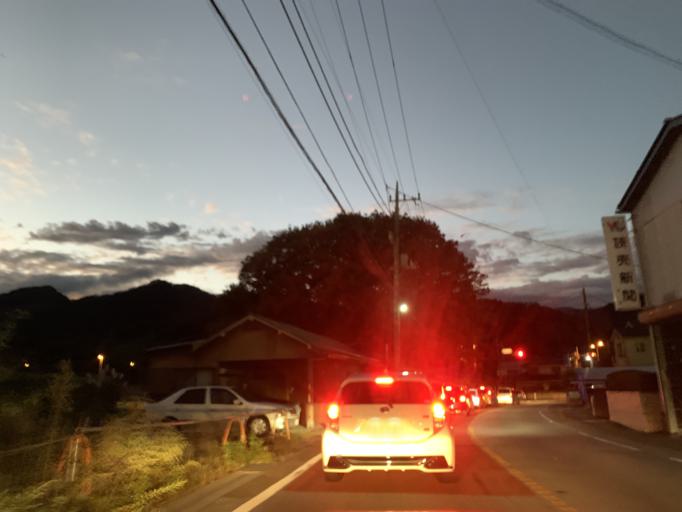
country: JP
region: Yamanashi
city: Otsuki
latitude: 35.6089
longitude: 138.9380
